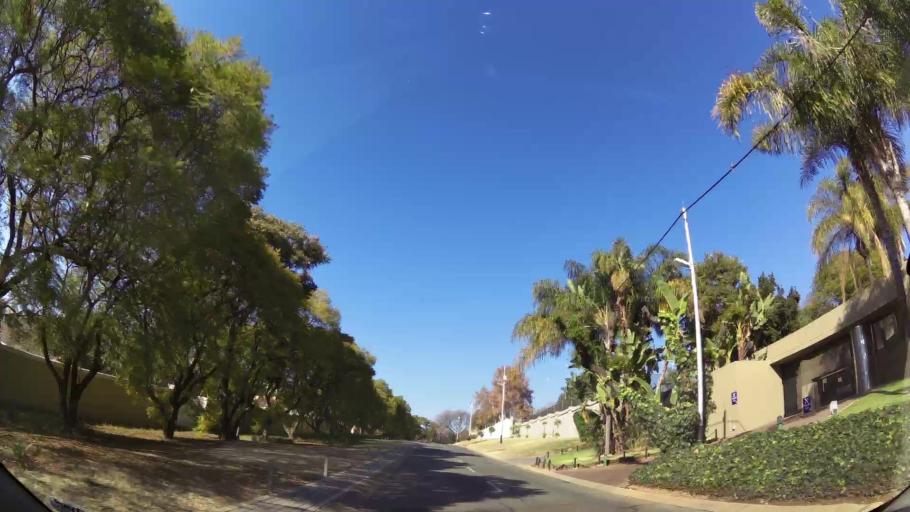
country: ZA
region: Gauteng
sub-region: City of Johannesburg Metropolitan Municipality
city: Midrand
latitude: -26.0506
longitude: 28.0338
